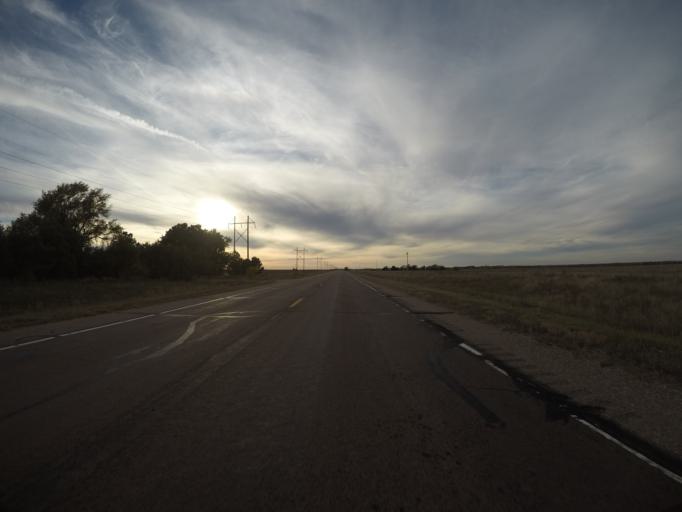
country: US
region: Colorado
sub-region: Yuma County
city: Yuma
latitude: 39.6551
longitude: -102.8199
